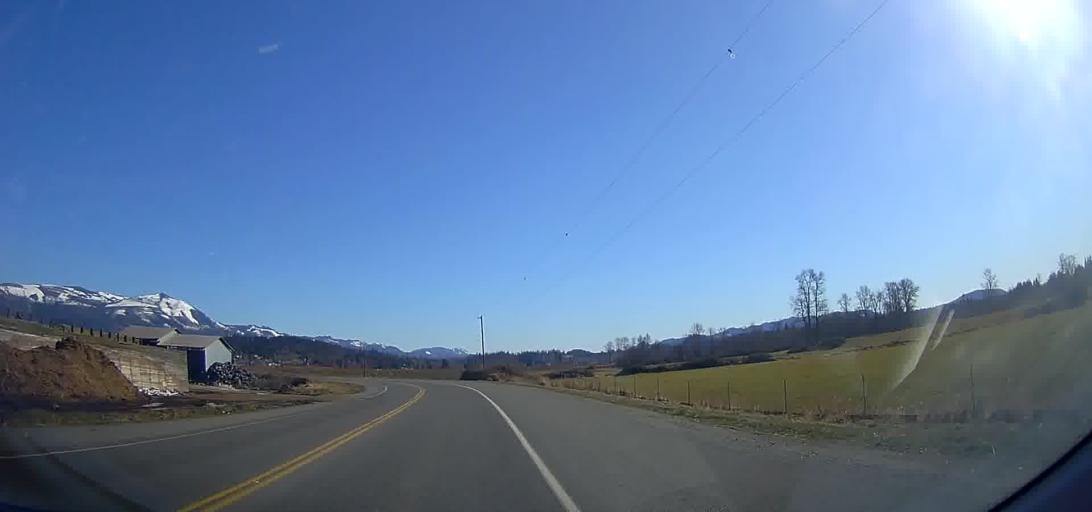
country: US
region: Washington
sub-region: Skagit County
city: Clear Lake
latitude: 48.4659
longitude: -122.2735
